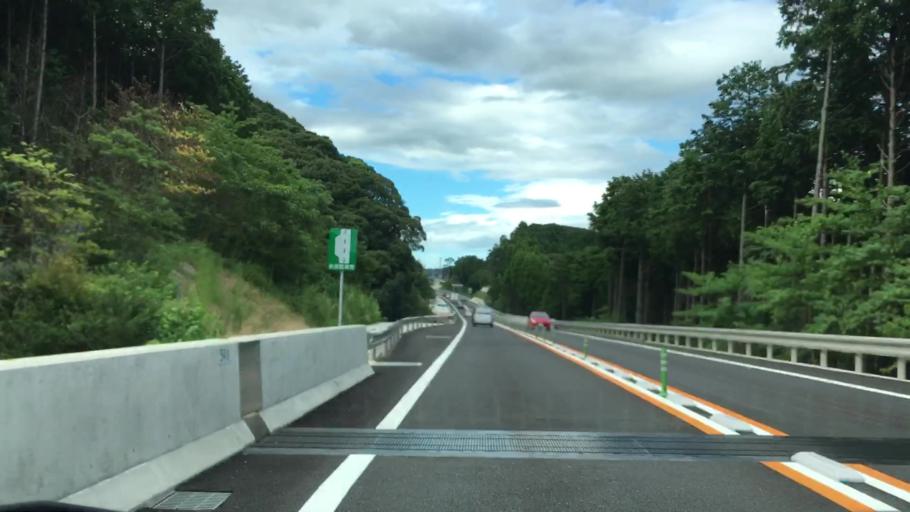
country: JP
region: Saga Prefecture
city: Imaricho-ko
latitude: 33.3261
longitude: 129.9273
